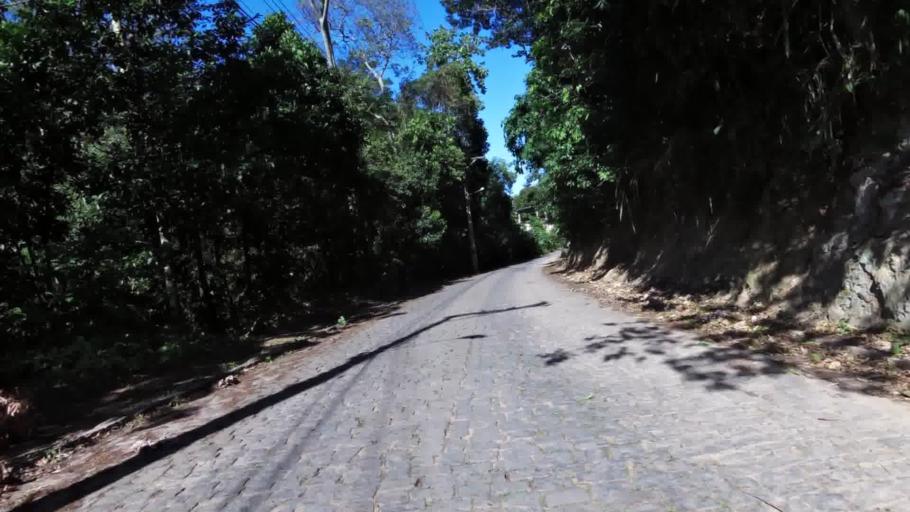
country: BR
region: Espirito Santo
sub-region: Rio Novo Do Sul
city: Rio Novo do Sul
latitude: -20.8541
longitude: -40.9242
